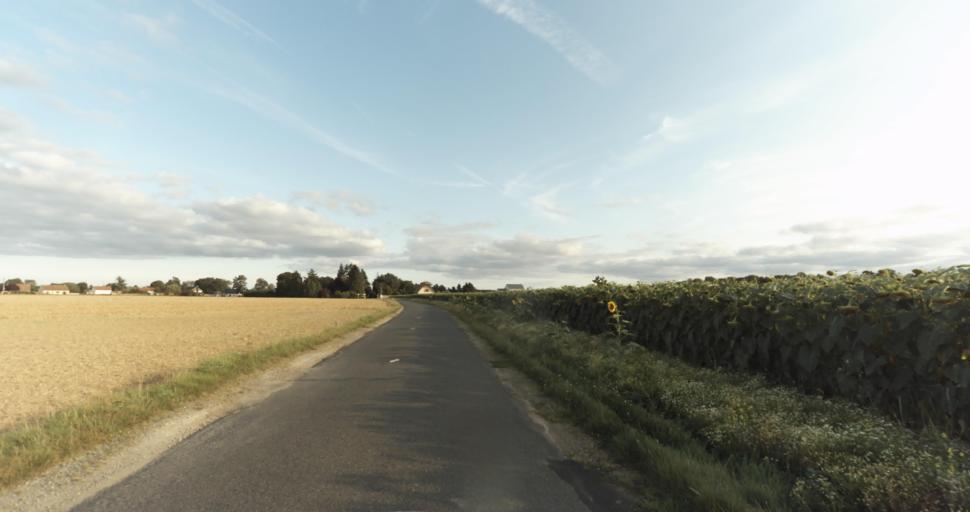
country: FR
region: Haute-Normandie
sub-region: Departement de l'Eure
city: Marcilly-sur-Eure
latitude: 48.8412
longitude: 1.2790
